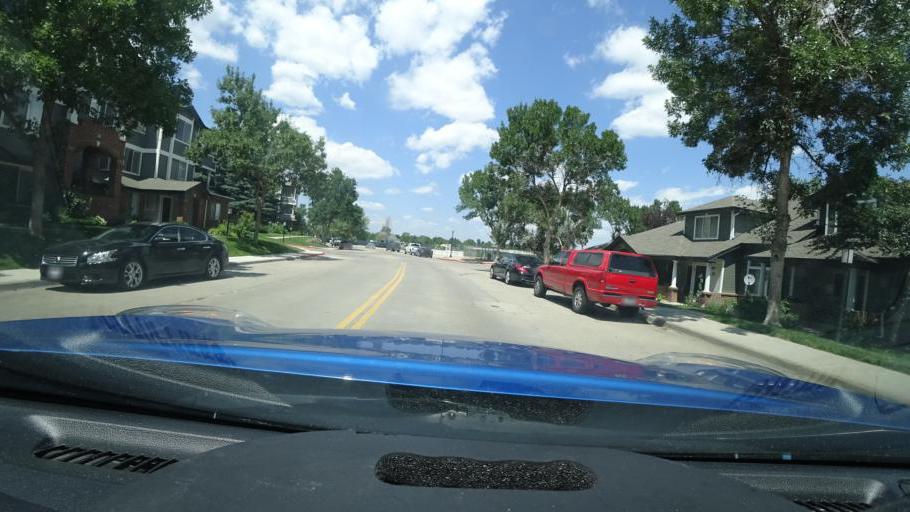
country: US
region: Colorado
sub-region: Arapahoe County
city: Glendale
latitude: 39.7003
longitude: -104.8900
